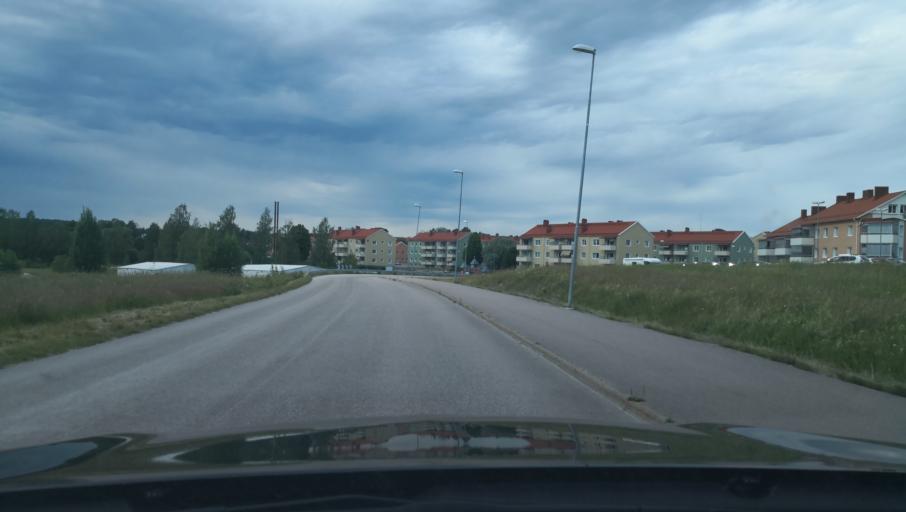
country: SE
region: Vaestmanland
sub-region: Fagersta Kommun
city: Fagersta
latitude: 59.9847
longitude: 15.8254
